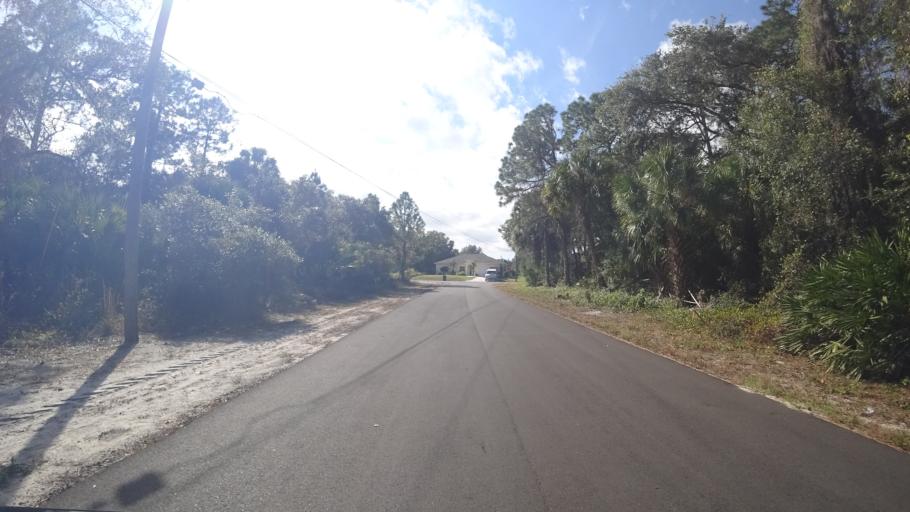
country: US
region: Florida
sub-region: Charlotte County
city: Port Charlotte
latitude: 27.0531
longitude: -82.1191
